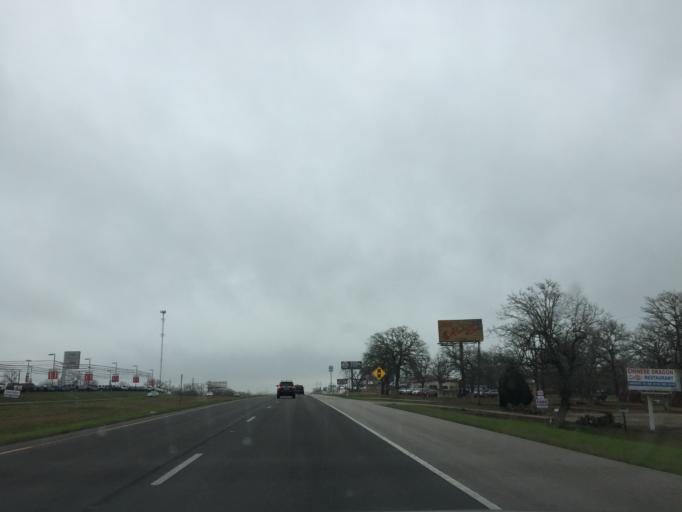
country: US
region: Texas
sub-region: Bastrop County
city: Wyldwood
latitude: 30.1259
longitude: -97.4393
